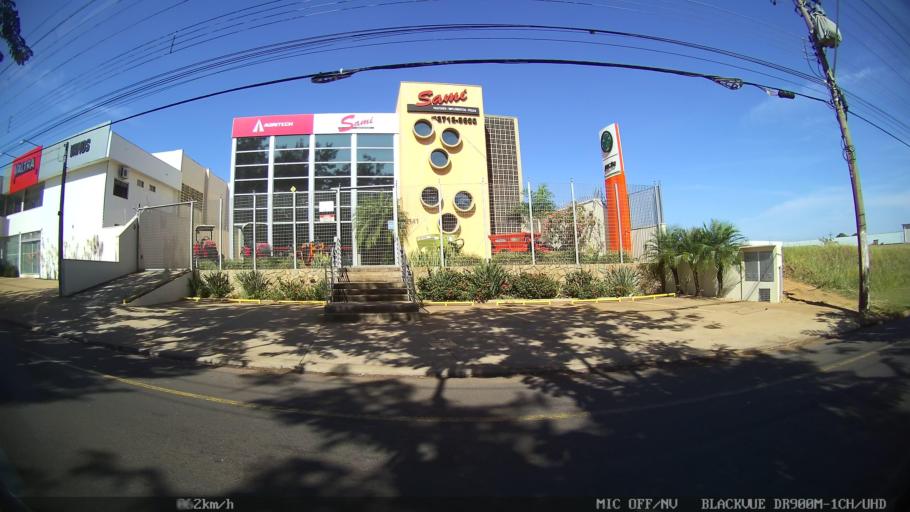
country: BR
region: Sao Paulo
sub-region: Franca
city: Franca
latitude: -20.5465
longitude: -47.4316
